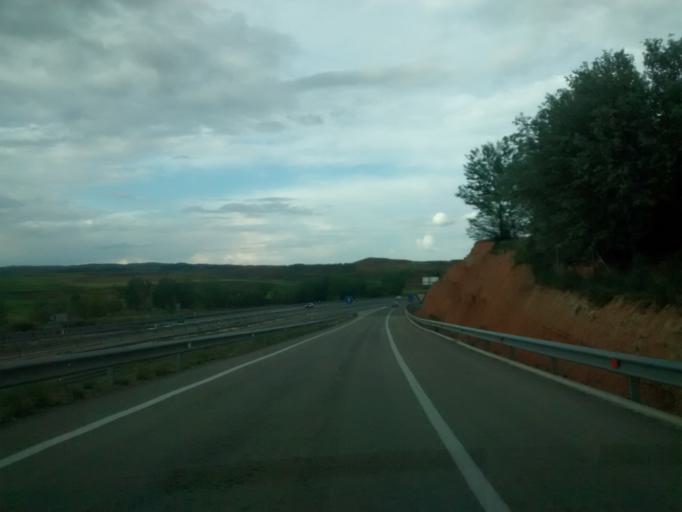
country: ES
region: Aragon
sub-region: Provincia de Zaragoza
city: Monreal de Ariza
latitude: 41.3081
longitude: -2.1232
